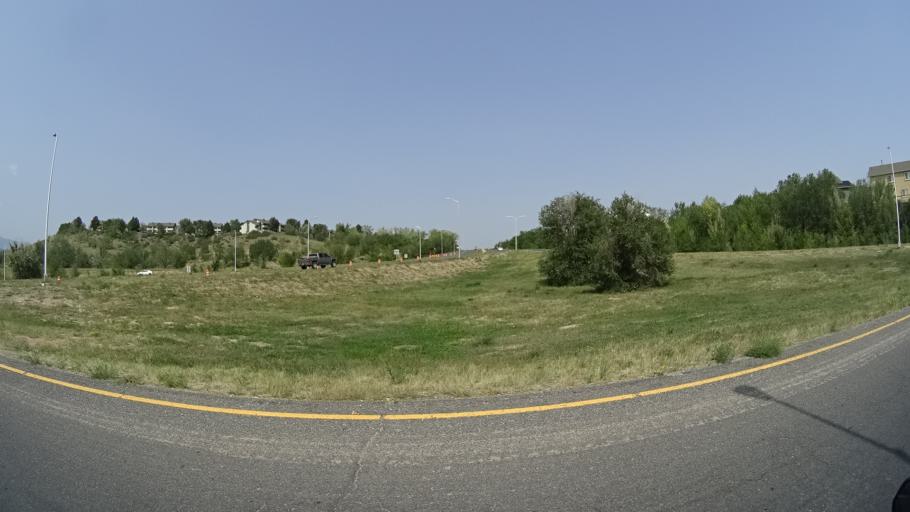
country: US
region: Colorado
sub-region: El Paso County
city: Stratmoor
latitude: 38.7998
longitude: -104.7802
